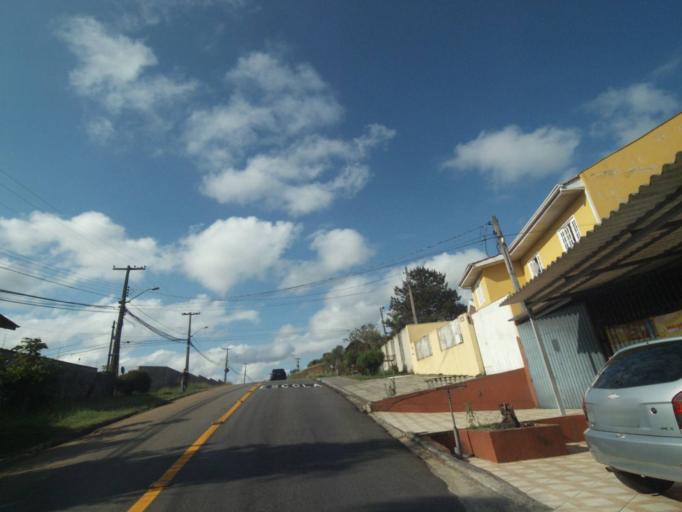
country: BR
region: Parana
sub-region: Curitiba
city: Curitiba
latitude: -25.3938
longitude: -49.3014
